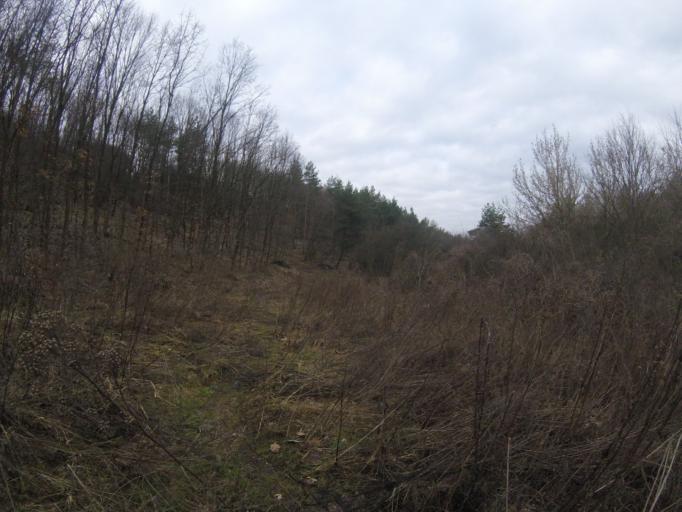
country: HU
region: Heves
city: Egerszalok
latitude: 47.8513
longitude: 20.3375
